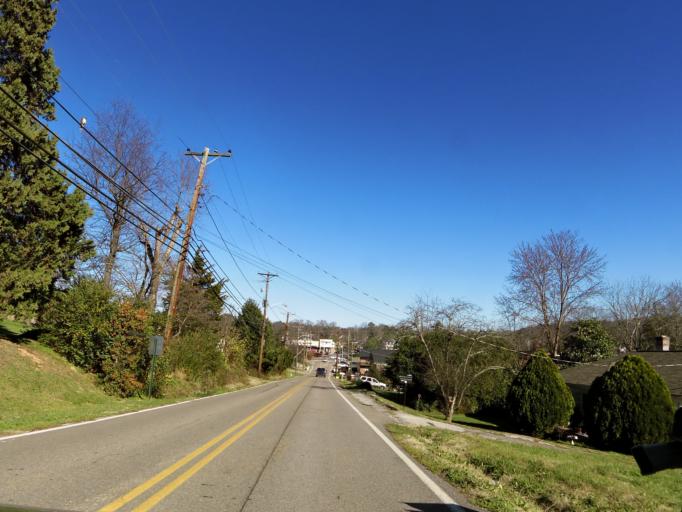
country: US
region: Tennessee
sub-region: Knox County
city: Knoxville
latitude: 36.0287
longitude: -83.9315
